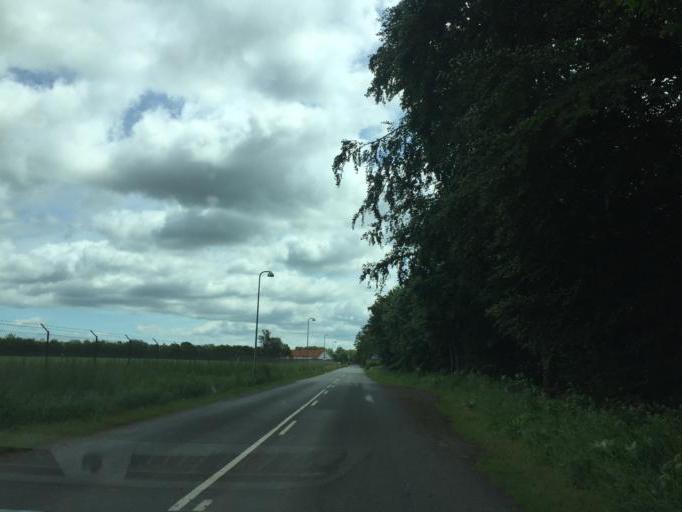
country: DK
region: South Denmark
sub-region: Odense Kommune
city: Hojby
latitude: 55.3568
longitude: 10.4328
